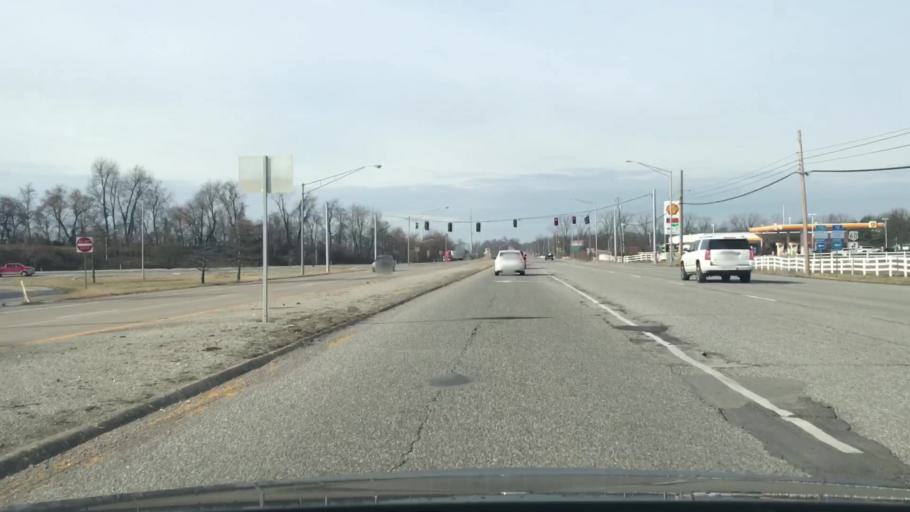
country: US
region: Kentucky
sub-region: Daviess County
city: Owensboro
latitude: 37.7747
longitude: -87.1642
